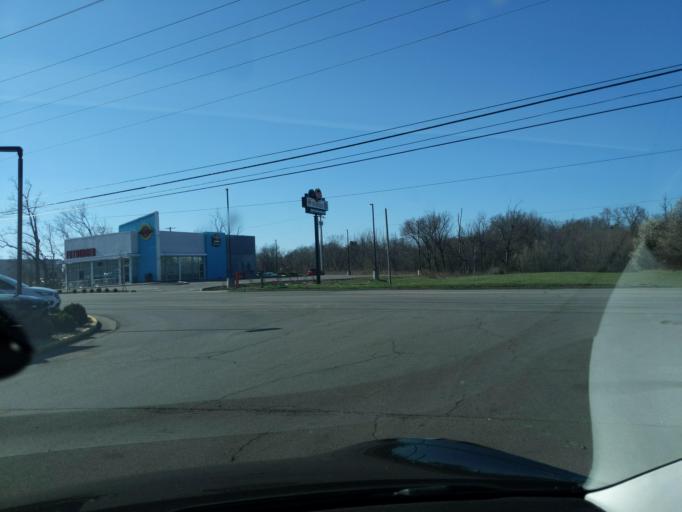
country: US
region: Kentucky
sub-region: Clark County
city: Winchester
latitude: 38.0056
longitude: -84.2073
